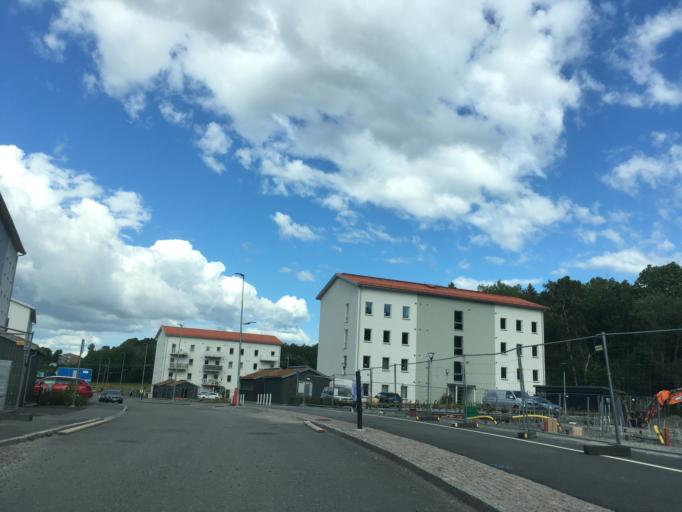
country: SE
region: Vaestra Goetaland
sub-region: Kungalvs Kommun
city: Kungalv
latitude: 57.8596
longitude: 11.9031
